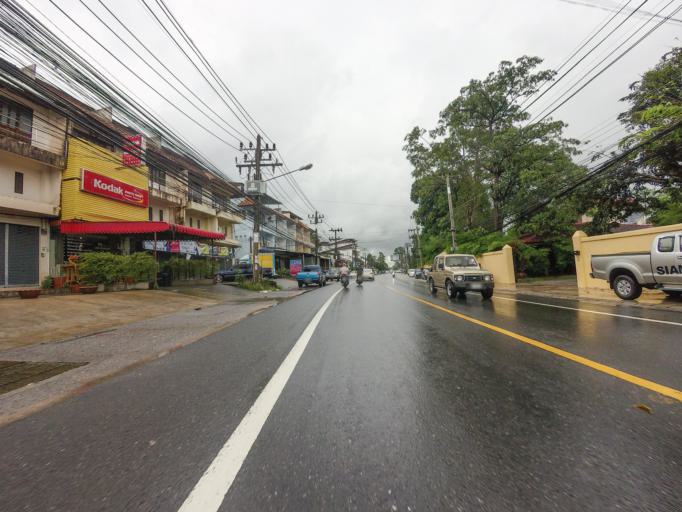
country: TH
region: Surat Thani
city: Ko Samui
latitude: 9.5121
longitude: 100.0512
